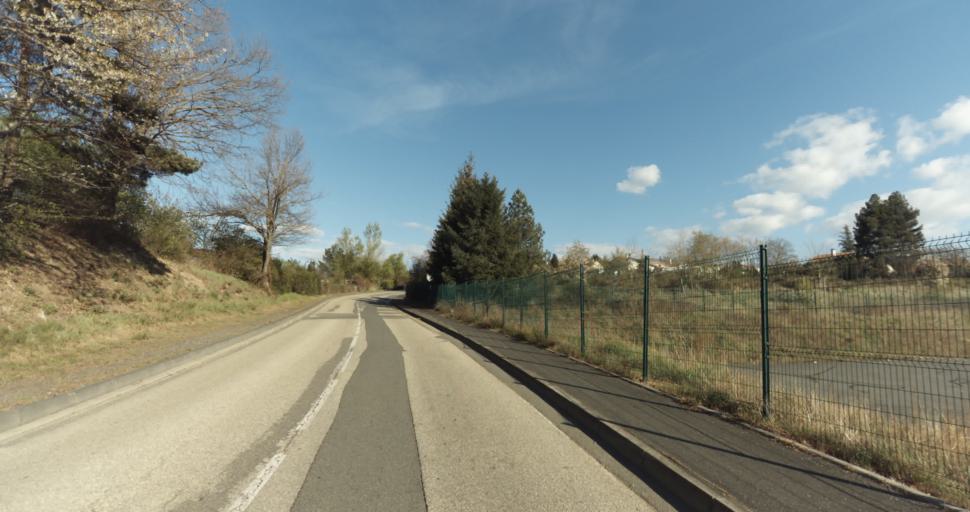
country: FR
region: Rhone-Alpes
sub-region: Departement de la Loire
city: Saint-Jean-Bonnefonds
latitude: 45.4534
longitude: 4.4266
